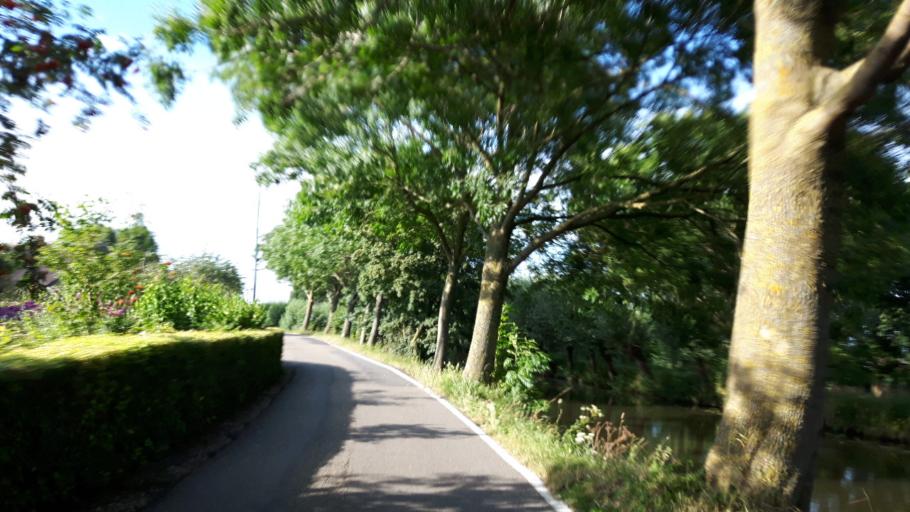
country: NL
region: Utrecht
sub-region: Gemeente Oudewater
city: Oudewater
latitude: 52.0386
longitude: 4.8886
